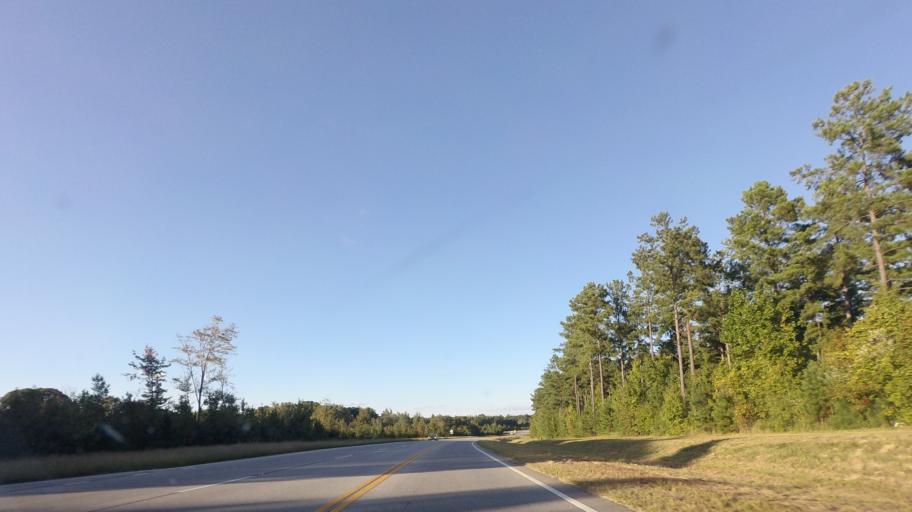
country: US
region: Georgia
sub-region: Spalding County
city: East Griffin
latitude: 33.2883
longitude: -84.1975
